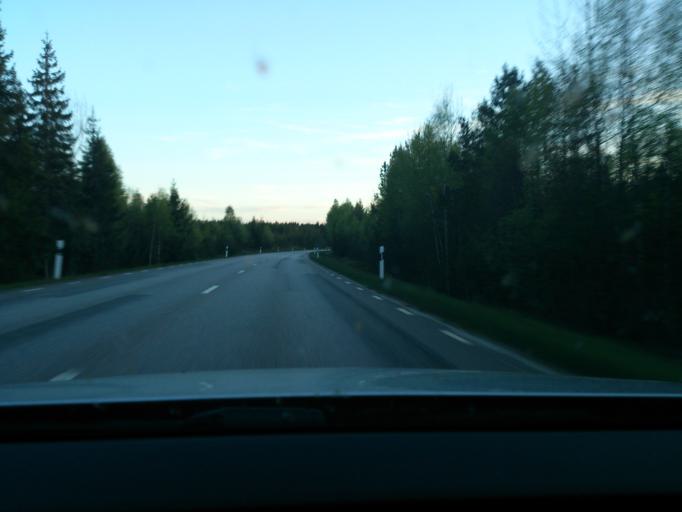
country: SE
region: Kronoberg
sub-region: Alvesta Kommun
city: Moheda
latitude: 57.0615
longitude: 14.6007
